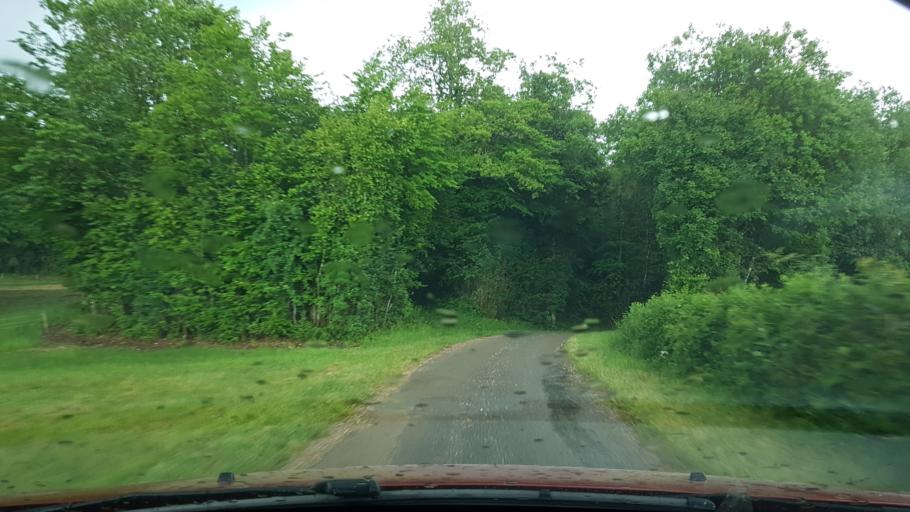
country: FR
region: Franche-Comte
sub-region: Departement du Jura
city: Clairvaux-les-Lacs
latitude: 46.5359
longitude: 5.7066
